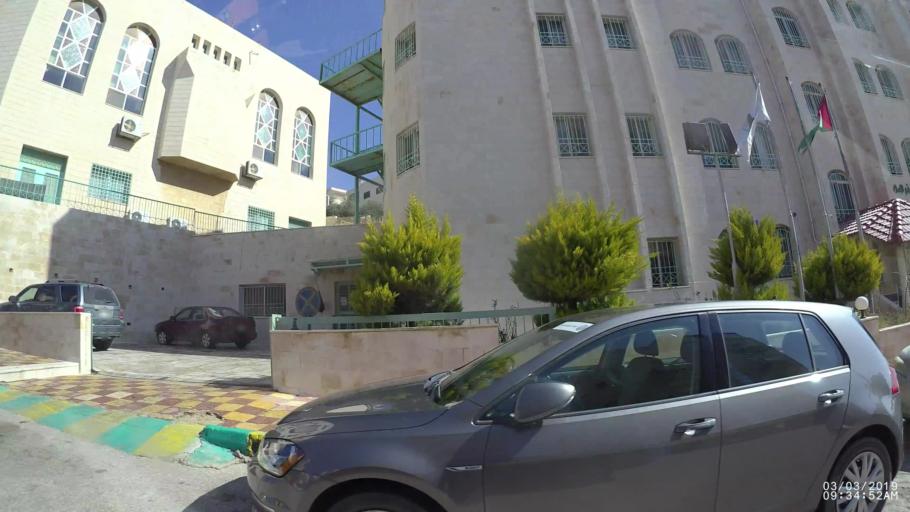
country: JO
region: Amman
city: Al Jubayhah
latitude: 31.9979
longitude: 35.8952
